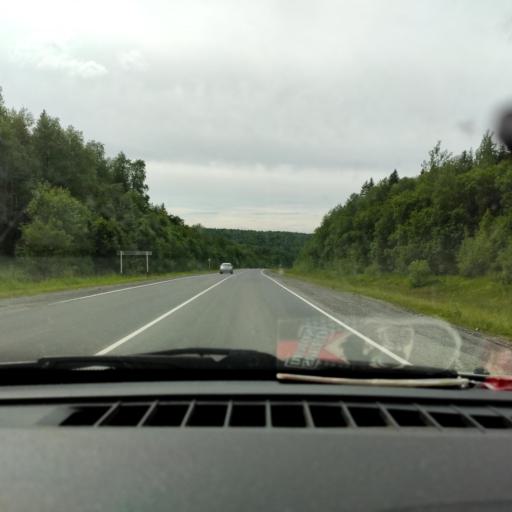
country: RU
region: Perm
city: Pashiya
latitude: 58.3730
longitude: 58.0523
